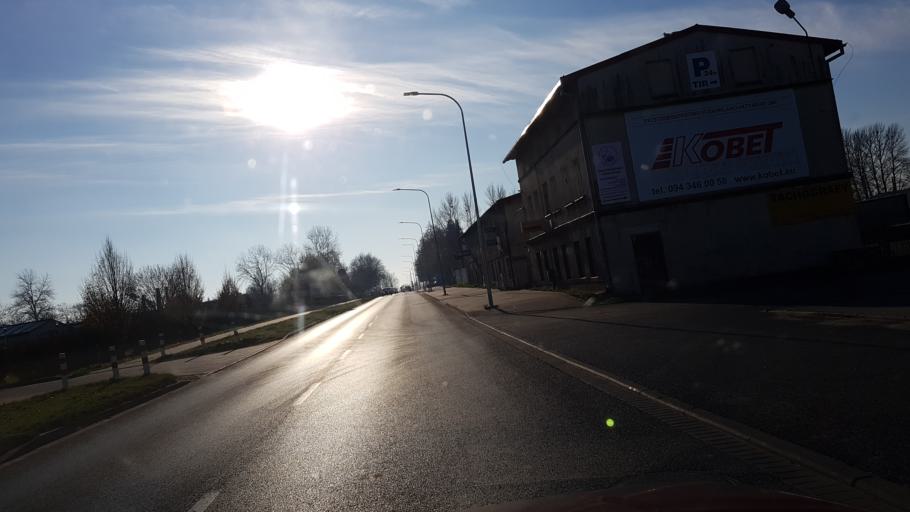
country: PL
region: West Pomeranian Voivodeship
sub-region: Koszalin
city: Koszalin
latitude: 54.1783
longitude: 16.1849
